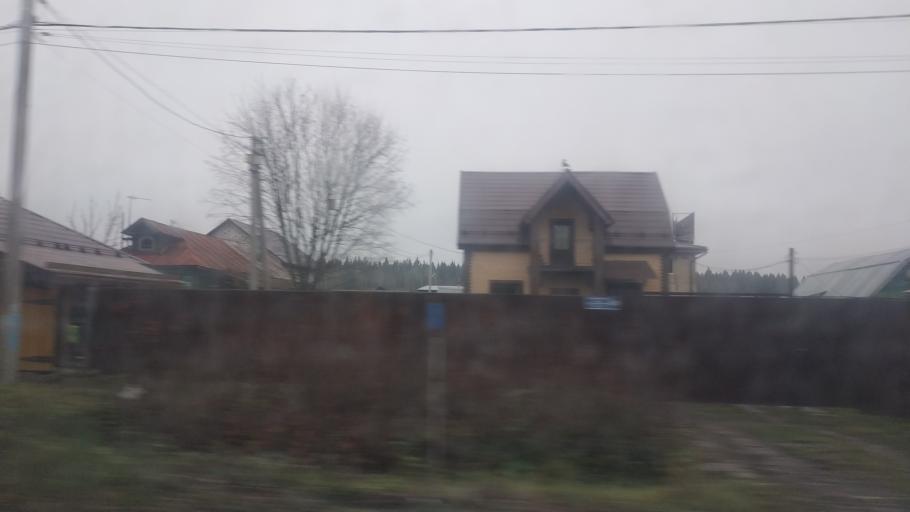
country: RU
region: Moskovskaya
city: Marfino
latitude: 56.0520
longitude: 37.5326
